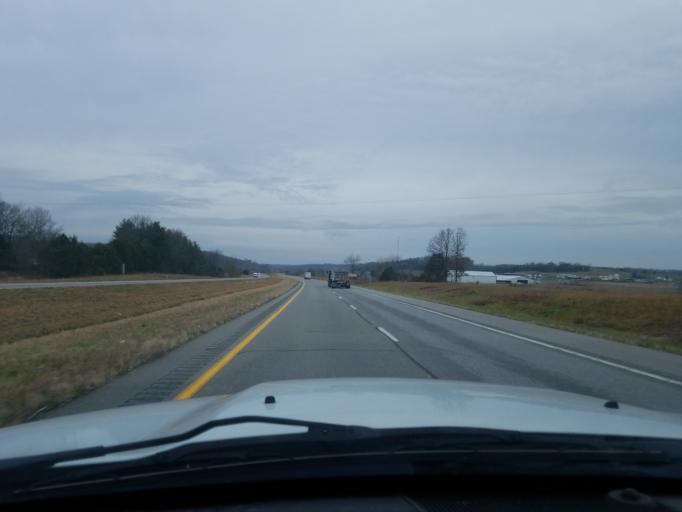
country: US
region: Indiana
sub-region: Harrison County
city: Corydon
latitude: 38.2422
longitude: -86.1733
